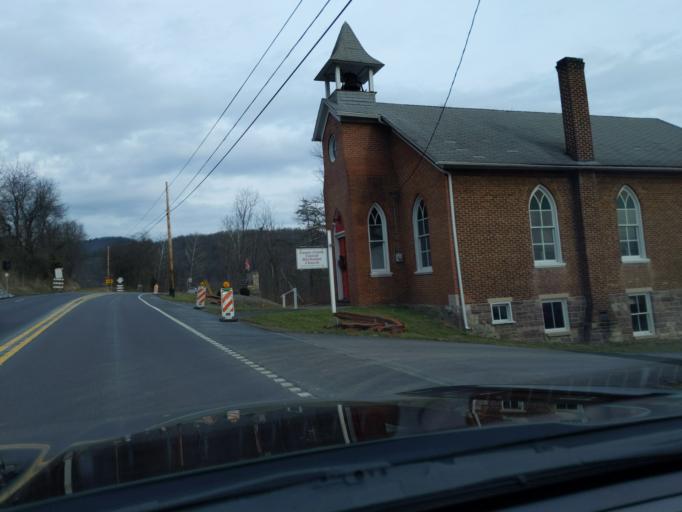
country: US
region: Pennsylvania
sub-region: Blair County
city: Williamsburg
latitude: 40.4748
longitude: -78.2778
